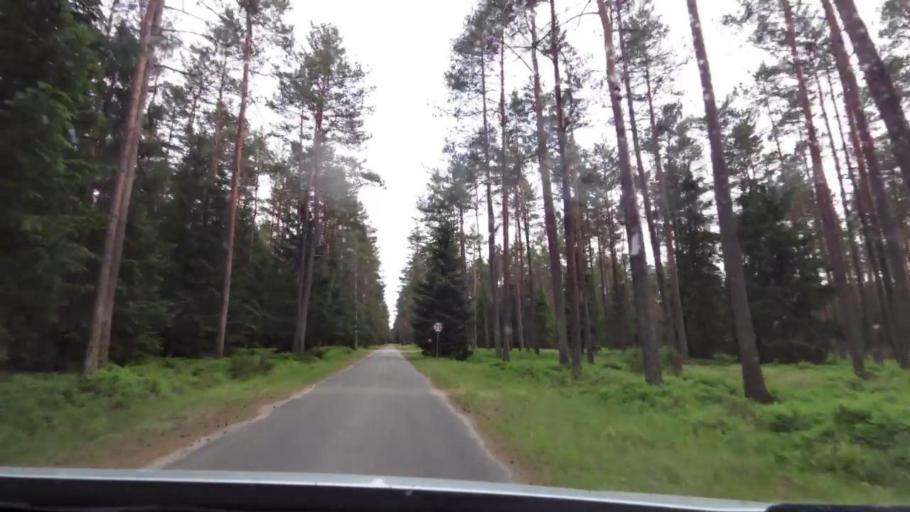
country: PL
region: Pomeranian Voivodeship
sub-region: Powiat bytowski
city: Trzebielino
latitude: 54.2164
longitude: 17.0036
